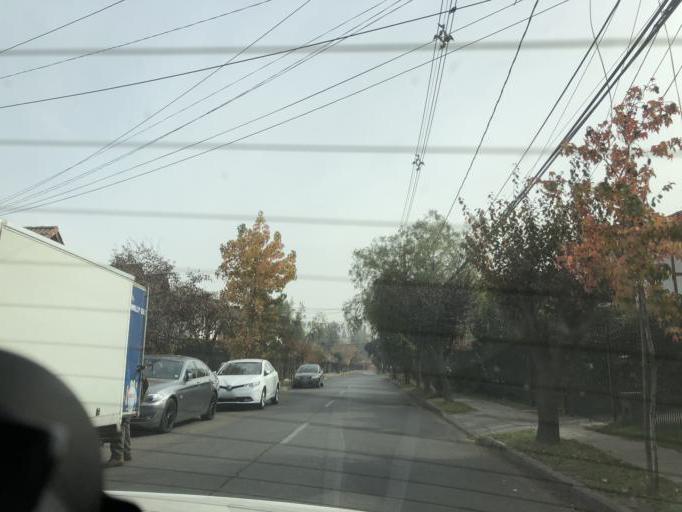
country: CL
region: Santiago Metropolitan
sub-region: Provincia de Cordillera
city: Puente Alto
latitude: -33.5501
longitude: -70.5647
